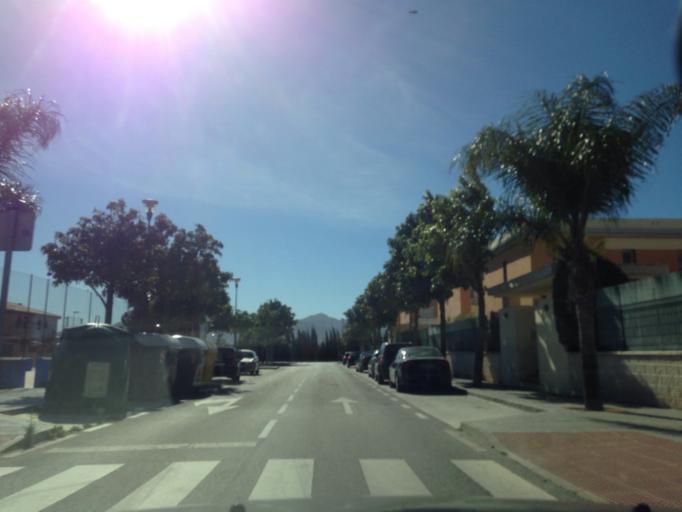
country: ES
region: Andalusia
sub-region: Provincia de Malaga
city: Alhaurin de la Torre
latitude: 36.7227
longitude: -4.5398
